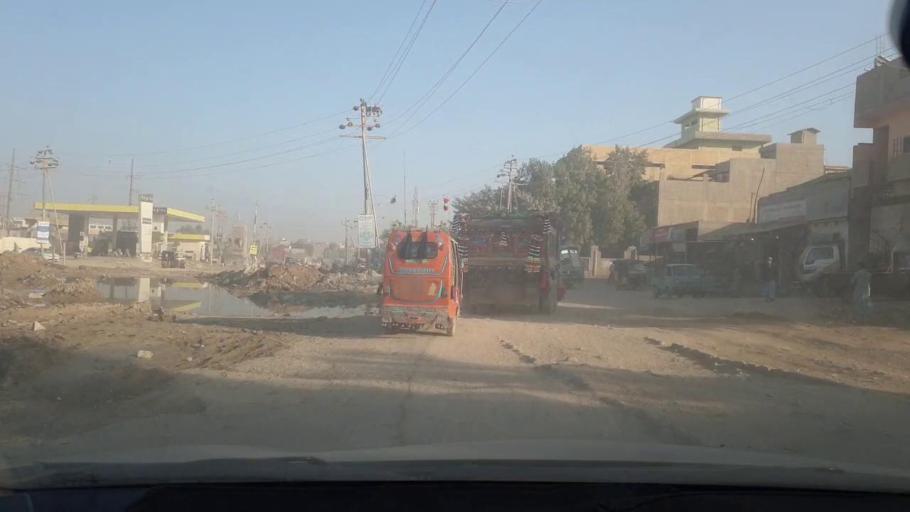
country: PK
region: Sindh
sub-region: Karachi District
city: Karachi
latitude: 24.9749
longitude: 67.0401
